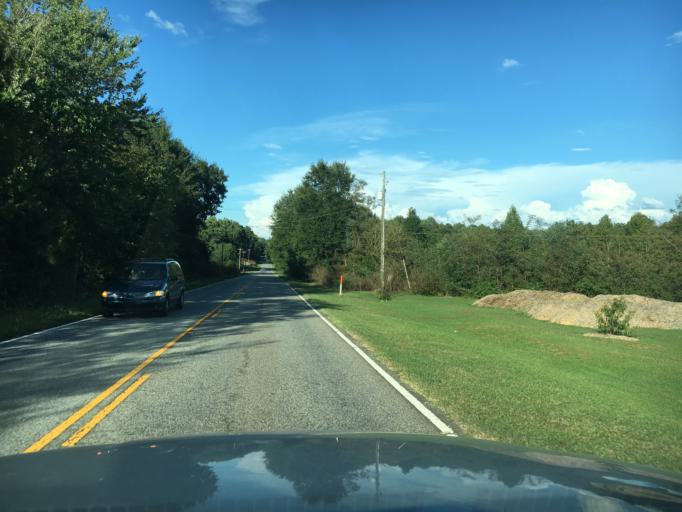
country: US
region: South Carolina
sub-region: Greenville County
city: Simpsonville
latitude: 34.7537
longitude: -82.2141
